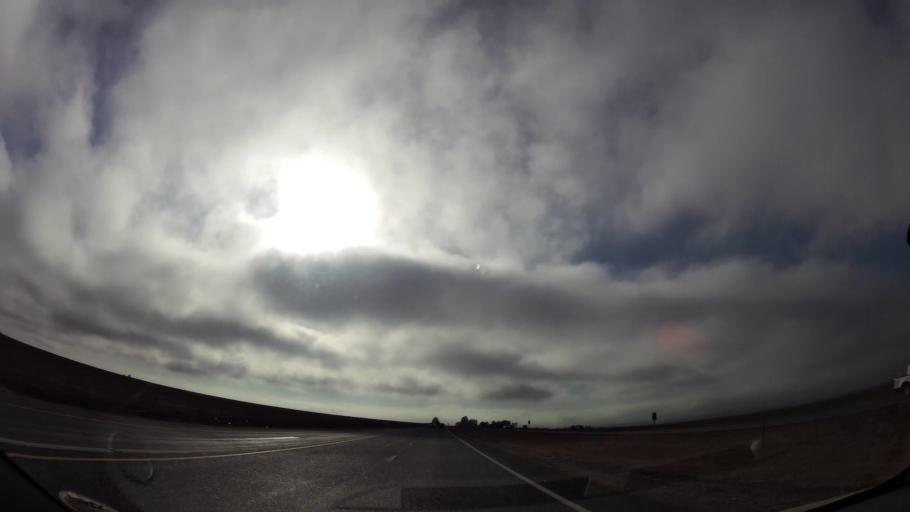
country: ZA
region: Mpumalanga
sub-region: Nkangala District Municipality
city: Delmas
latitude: -26.0427
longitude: 28.8371
